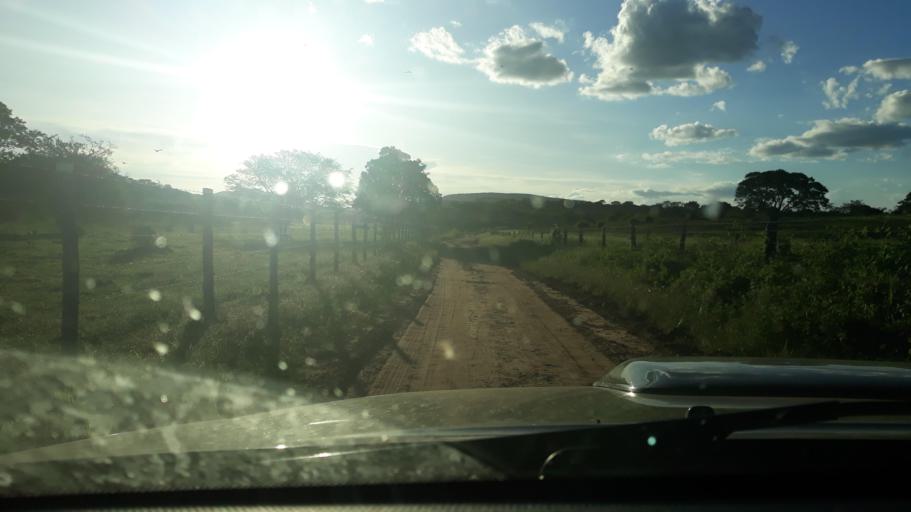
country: BR
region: Bahia
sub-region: Riacho De Santana
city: Riacho de Santana
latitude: -13.8458
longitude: -42.7547
